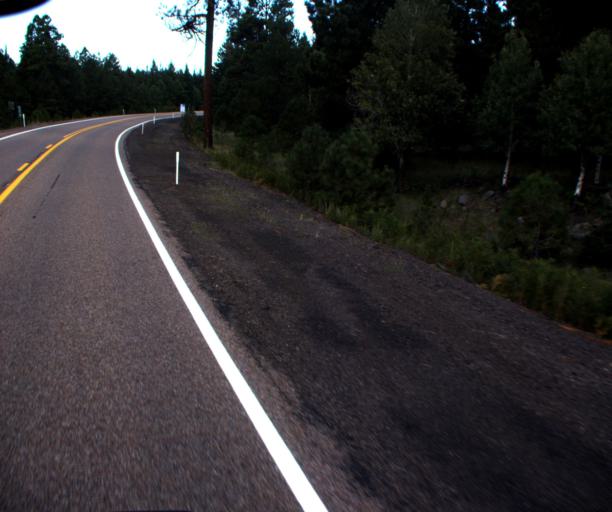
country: US
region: Arizona
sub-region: Navajo County
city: Pinetop-Lakeside
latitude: 34.0236
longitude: -109.6456
